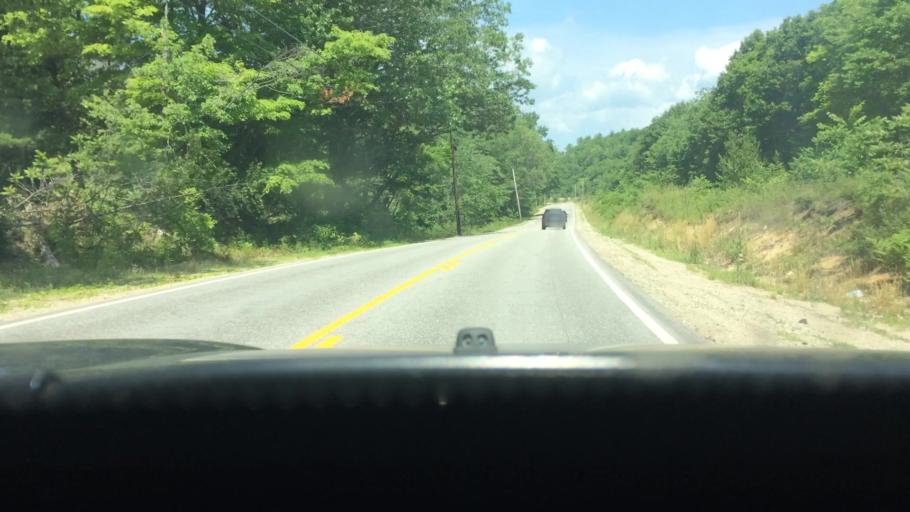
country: US
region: Maine
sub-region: Androscoggin County
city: Mechanic Falls
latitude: 44.1215
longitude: -70.4317
